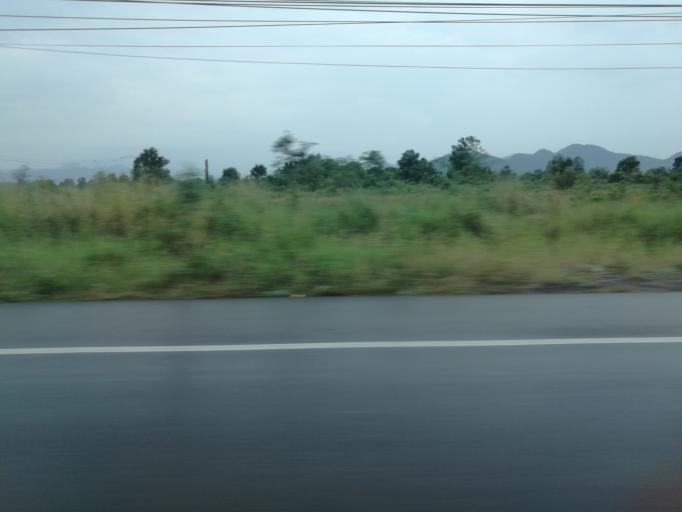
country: TH
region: Prachuap Khiri Khan
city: Kui Buri
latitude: 12.1138
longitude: 99.8530
